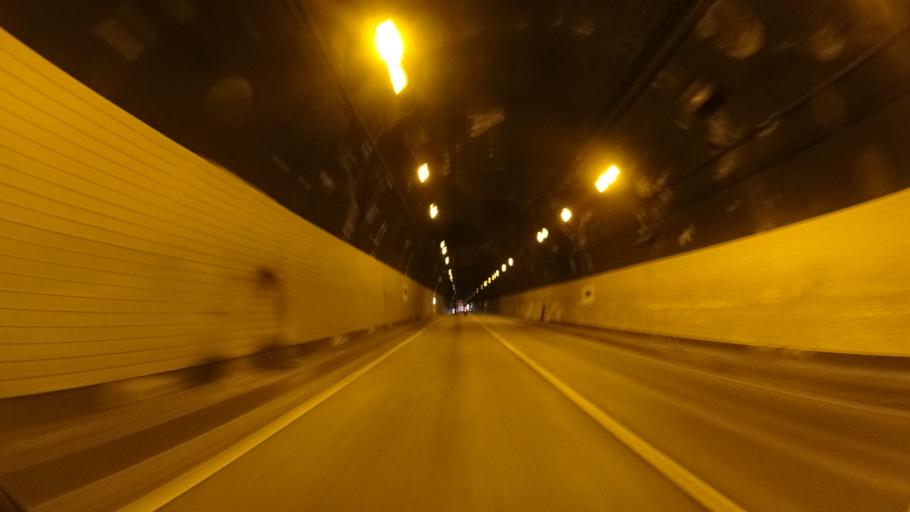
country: JP
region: Ehime
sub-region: Nishiuwa-gun
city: Ikata-cho
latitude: 33.4911
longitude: 132.3848
